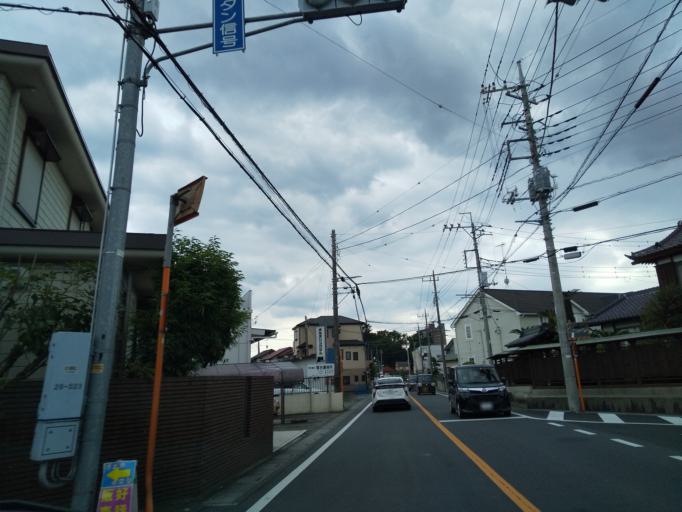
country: JP
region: Saitama
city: Kasukabe
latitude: 35.9842
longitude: 139.7651
